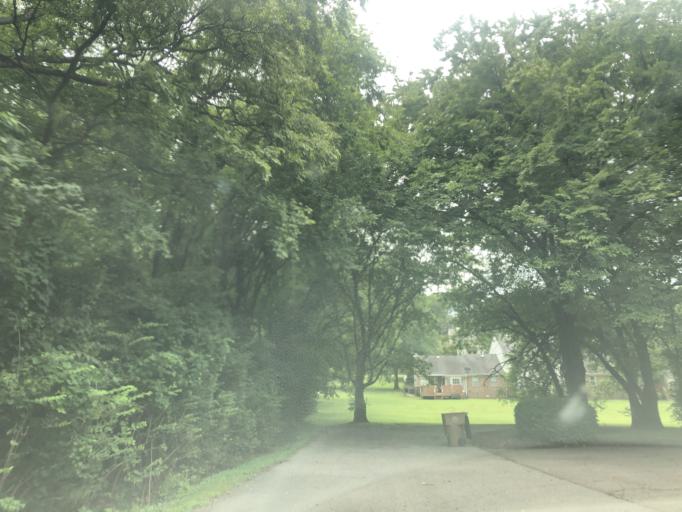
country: US
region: Tennessee
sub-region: Davidson County
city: Oak Hill
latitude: 36.0909
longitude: -86.7890
